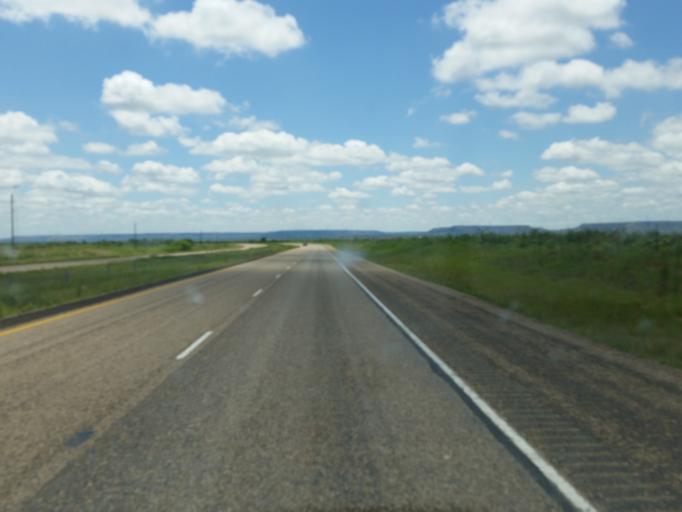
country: US
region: Texas
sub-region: Garza County
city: Post
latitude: 33.0780
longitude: -101.2389
